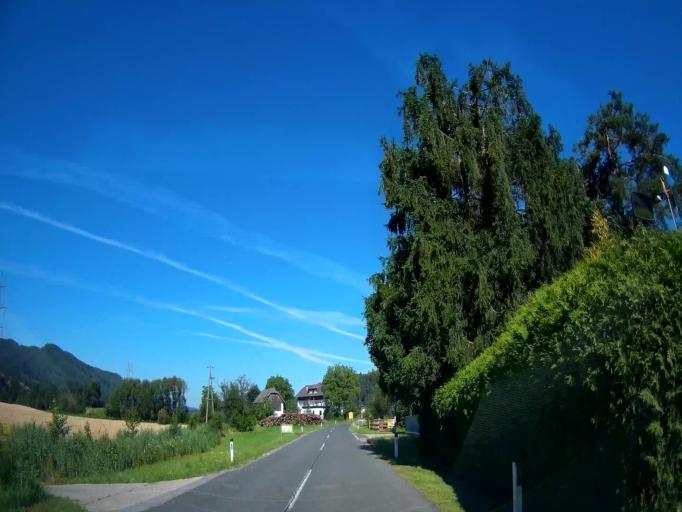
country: AT
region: Carinthia
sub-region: Politischer Bezirk Klagenfurt Land
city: Poggersdorf
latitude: 46.6895
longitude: 14.4931
